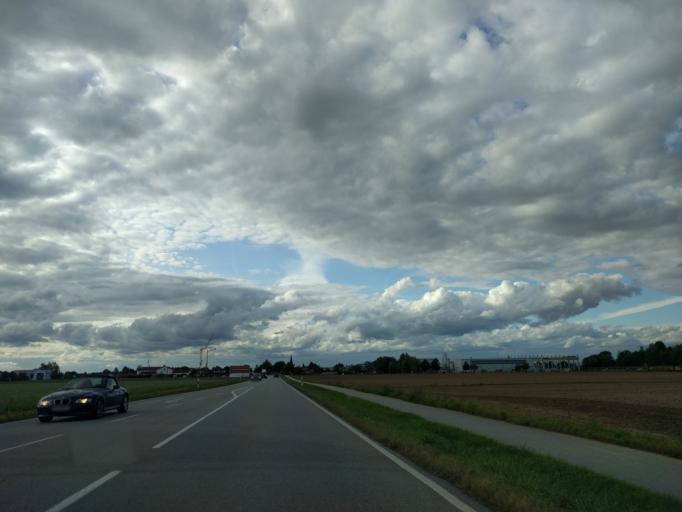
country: DE
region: Bavaria
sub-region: Lower Bavaria
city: Strasskirchen
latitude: 48.8255
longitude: 12.7354
